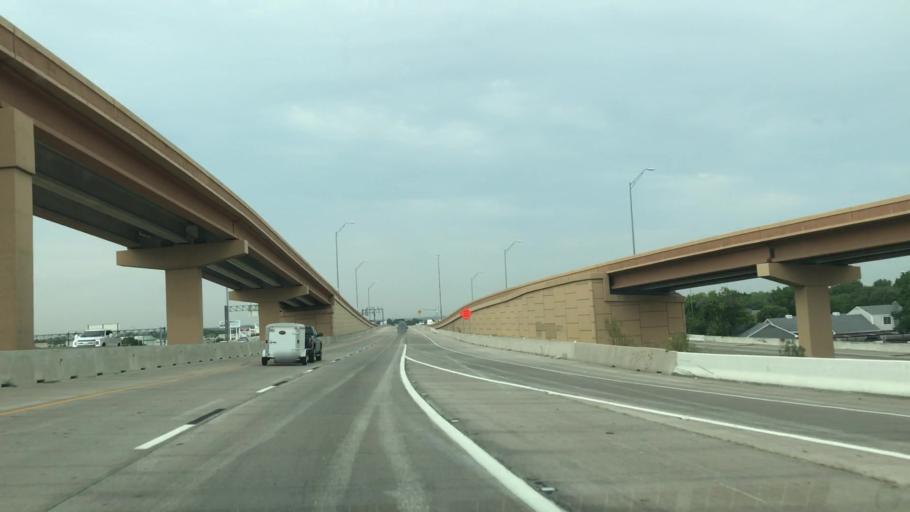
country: US
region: Texas
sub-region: Tarrant County
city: North Richland Hills
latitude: 32.8288
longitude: -97.2055
